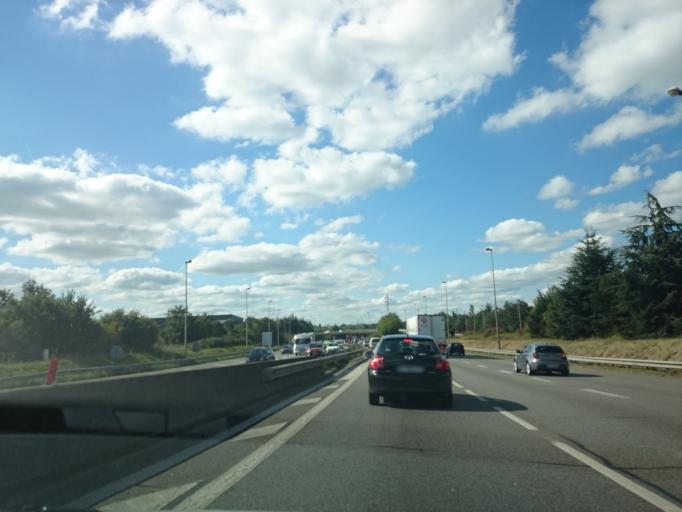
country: FR
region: Pays de la Loire
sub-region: Departement de la Loire-Atlantique
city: Bouguenais
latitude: 47.1994
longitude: -1.6168
